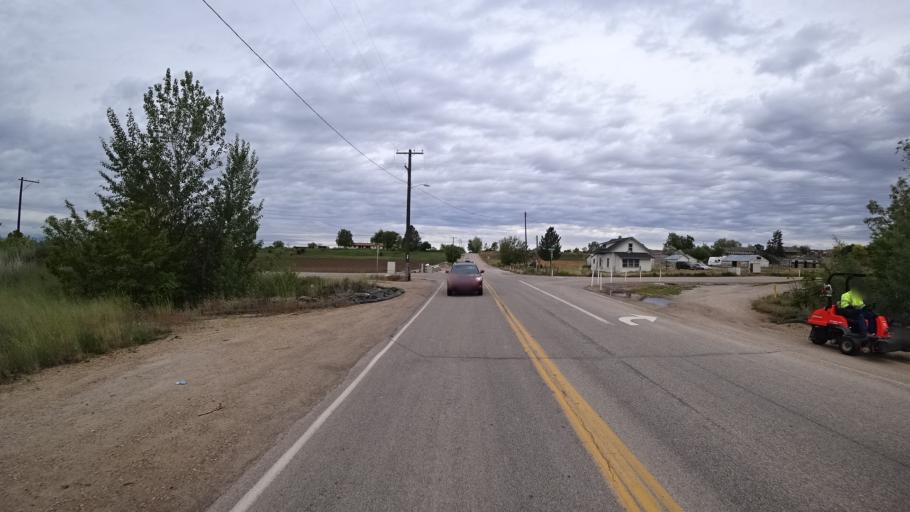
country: US
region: Idaho
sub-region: Ada County
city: Star
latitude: 43.7212
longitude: -116.4679
